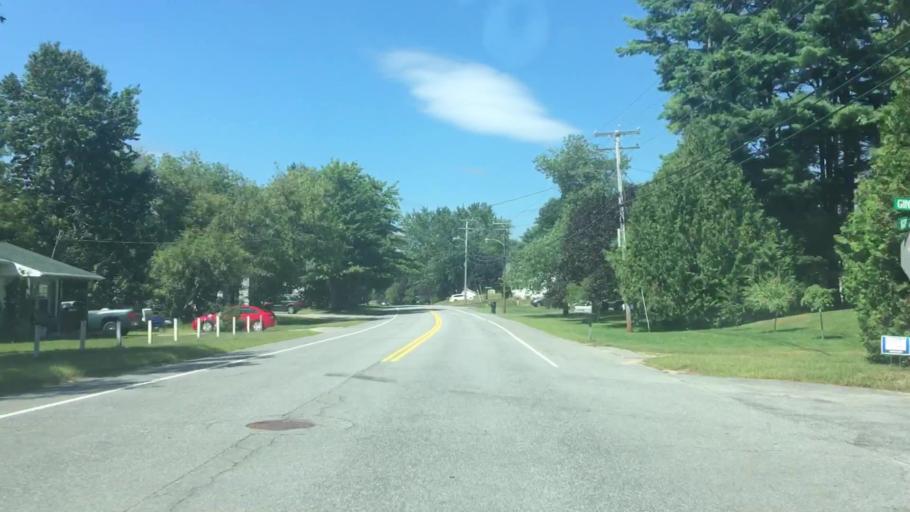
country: US
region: Maine
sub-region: Androscoggin County
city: Sabattus
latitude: 44.0910
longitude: -70.1478
